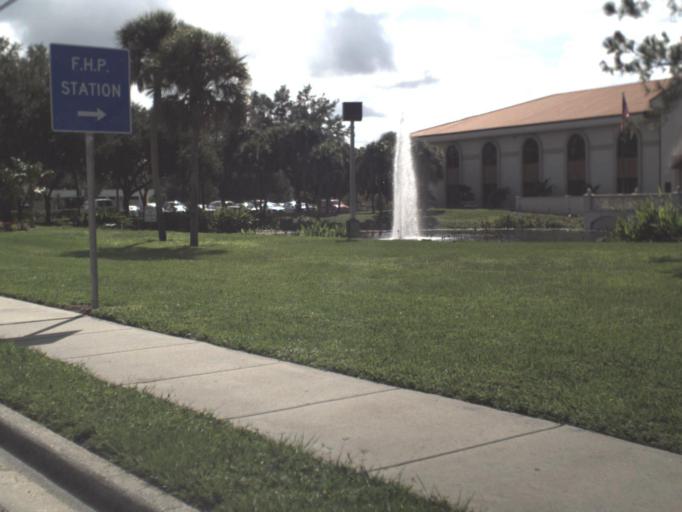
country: US
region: Florida
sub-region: Sarasota County
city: South Venice
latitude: 27.0497
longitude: -82.4010
